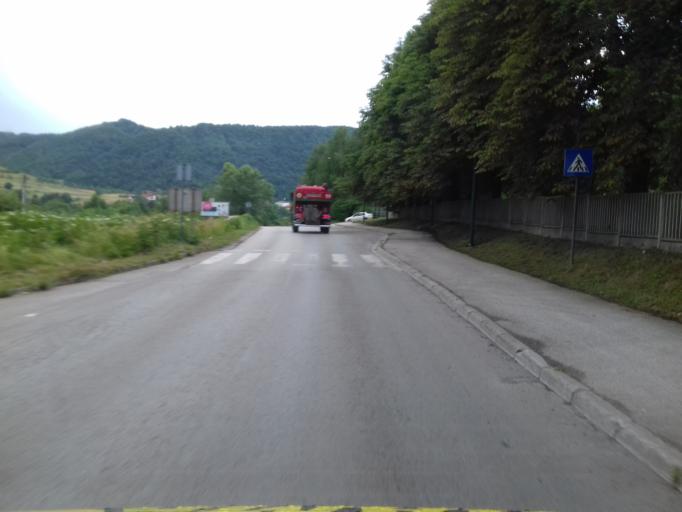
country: BA
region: Federation of Bosnia and Herzegovina
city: Visoko
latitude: 43.9774
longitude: 18.1862
